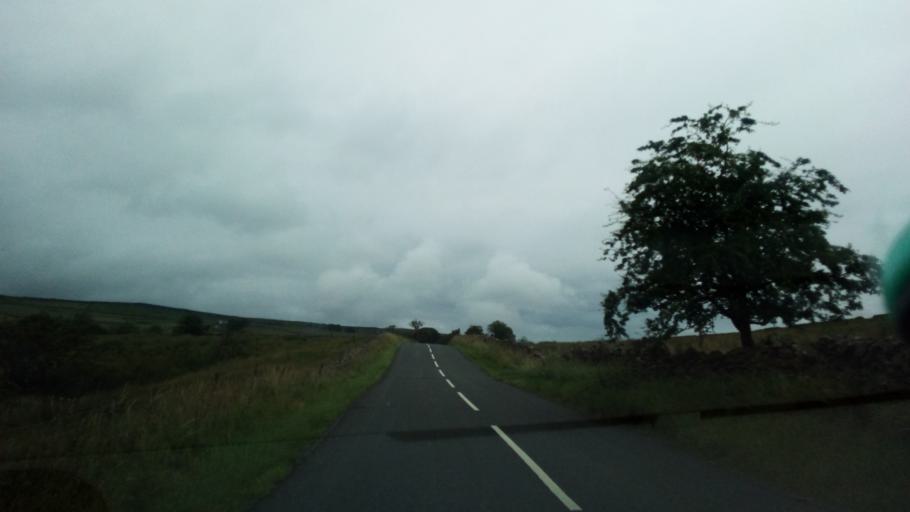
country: GB
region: England
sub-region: Cumbria
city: Kirkby Stephen
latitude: 54.5395
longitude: -2.2925
